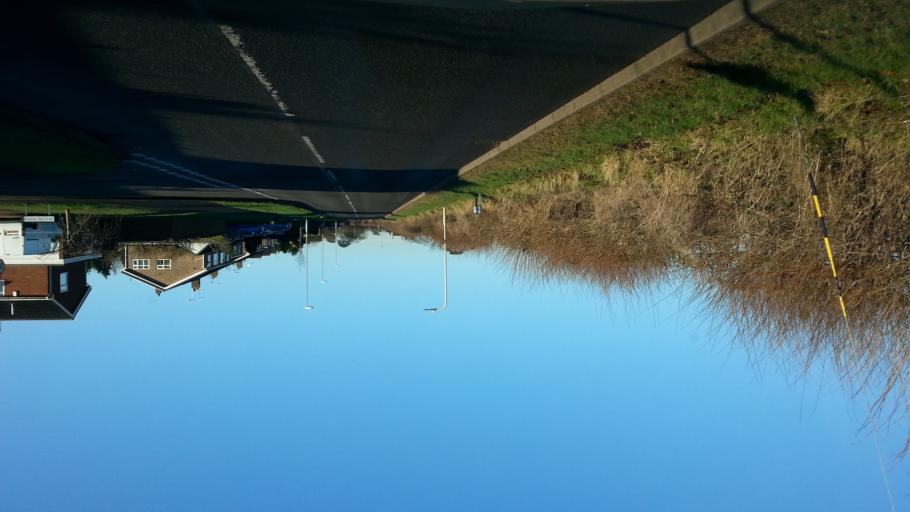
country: GB
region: England
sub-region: Leicestershire
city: Queniborough
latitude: 52.7171
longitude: -1.0501
